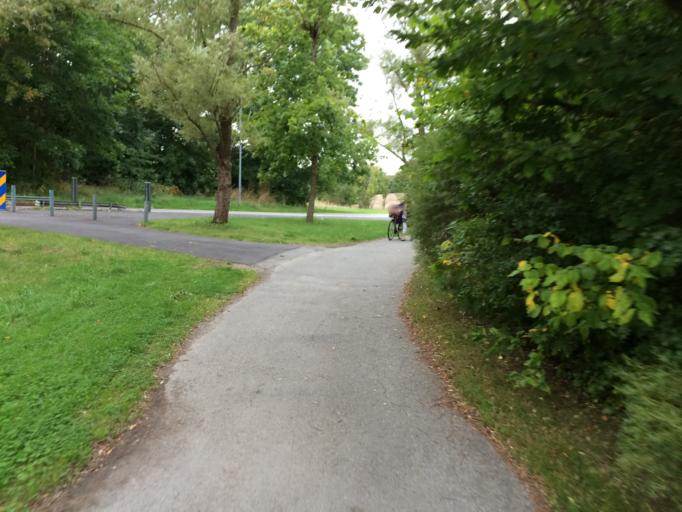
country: SE
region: Skane
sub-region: Lunds Kommun
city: Lund
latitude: 55.7125
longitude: 13.2319
